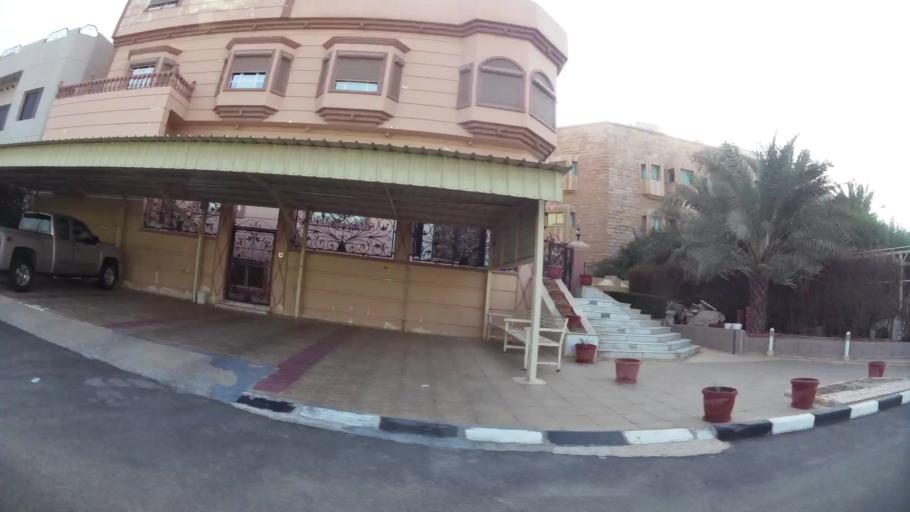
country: KW
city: Al Funaytis
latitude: 29.2312
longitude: 48.0796
